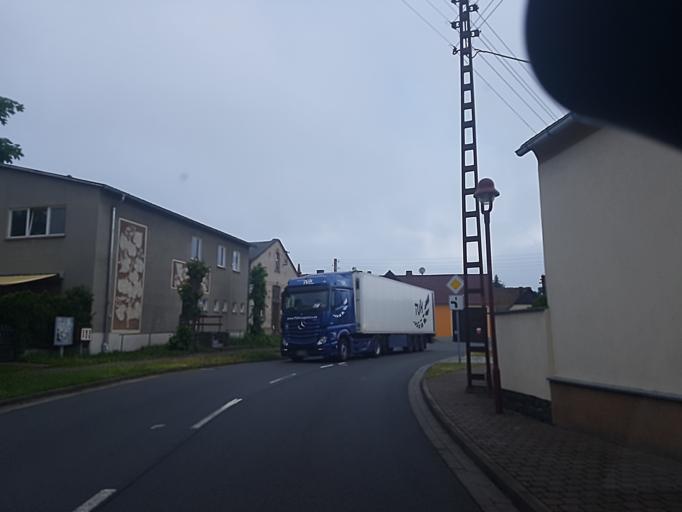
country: DE
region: Saxony-Anhalt
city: Klieken
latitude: 51.9678
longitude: 12.3435
